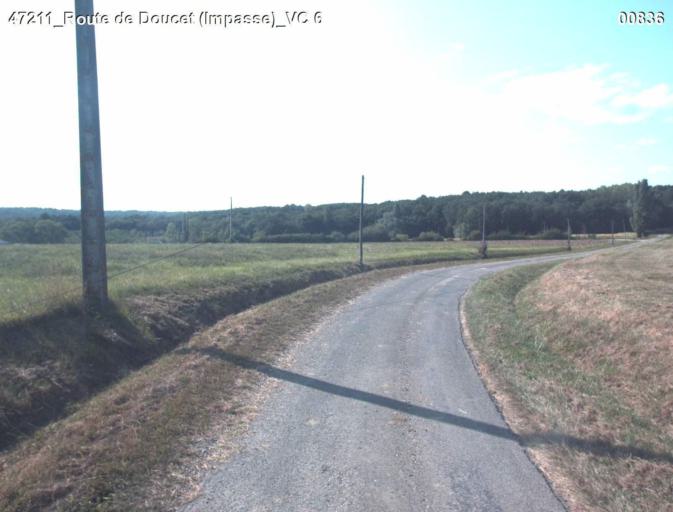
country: FR
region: Midi-Pyrenees
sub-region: Departement du Gers
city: Montreal
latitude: 44.0155
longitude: 0.2023
